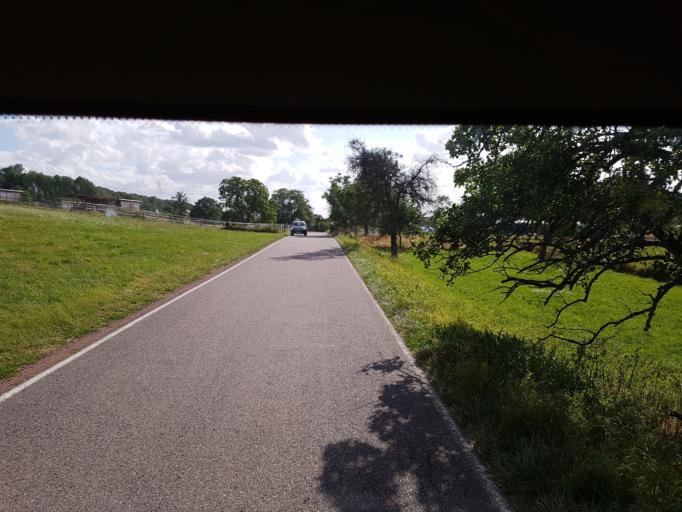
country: DE
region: Rheinland-Pfalz
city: Kirf
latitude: 49.5361
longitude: 6.4390
